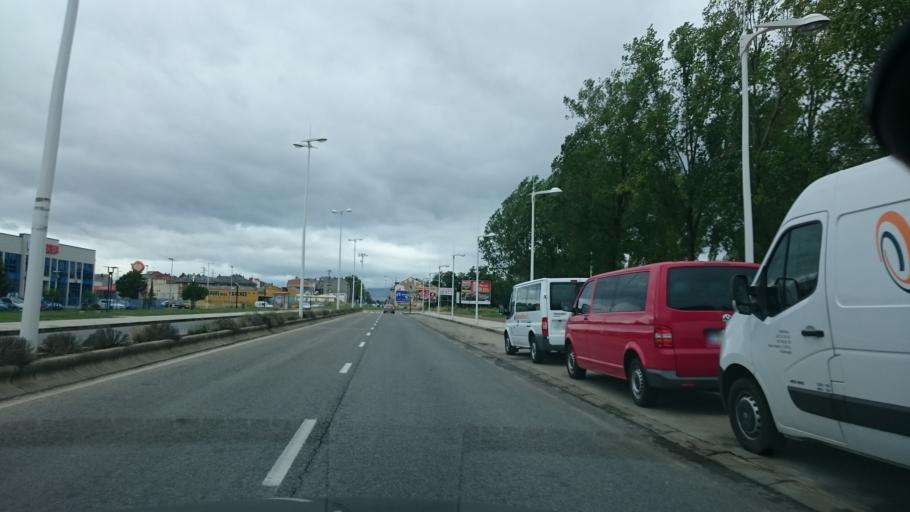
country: ES
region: Castille and Leon
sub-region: Provincia de Leon
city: Ponferrada
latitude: 42.5555
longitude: -6.6142
